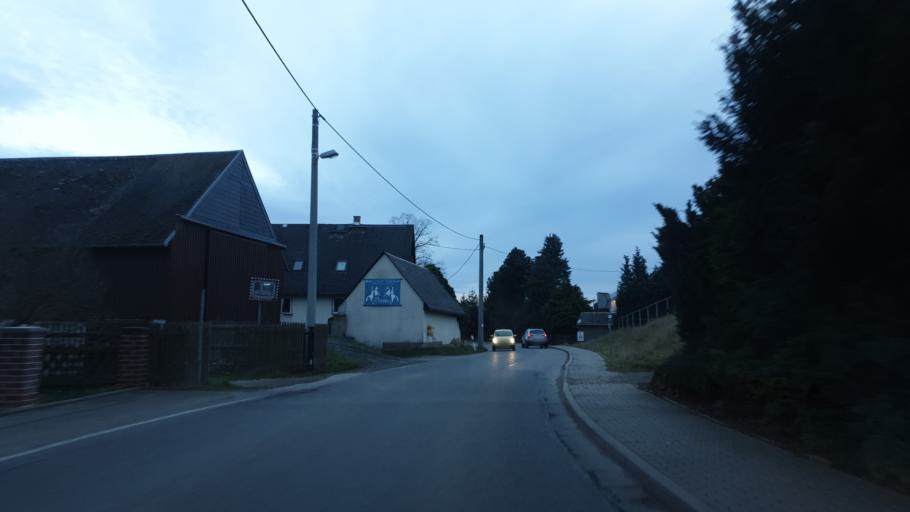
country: DE
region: Saxony
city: Hartenstein
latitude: 50.6892
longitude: 12.6707
